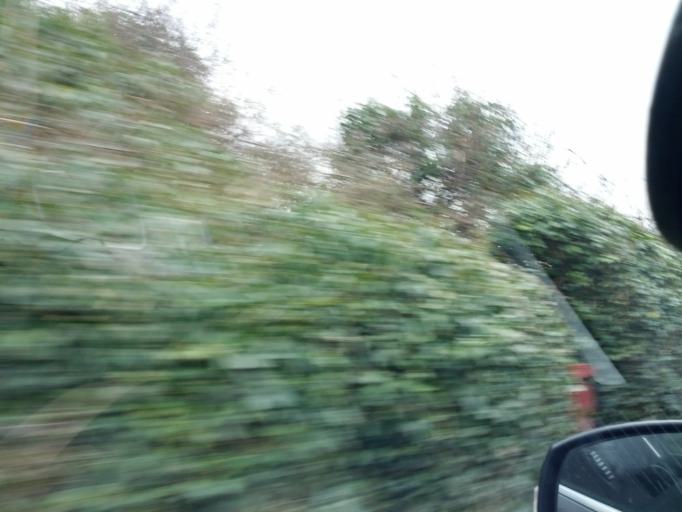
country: IE
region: Connaught
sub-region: County Galway
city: Oranmore
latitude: 53.2001
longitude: -8.9183
